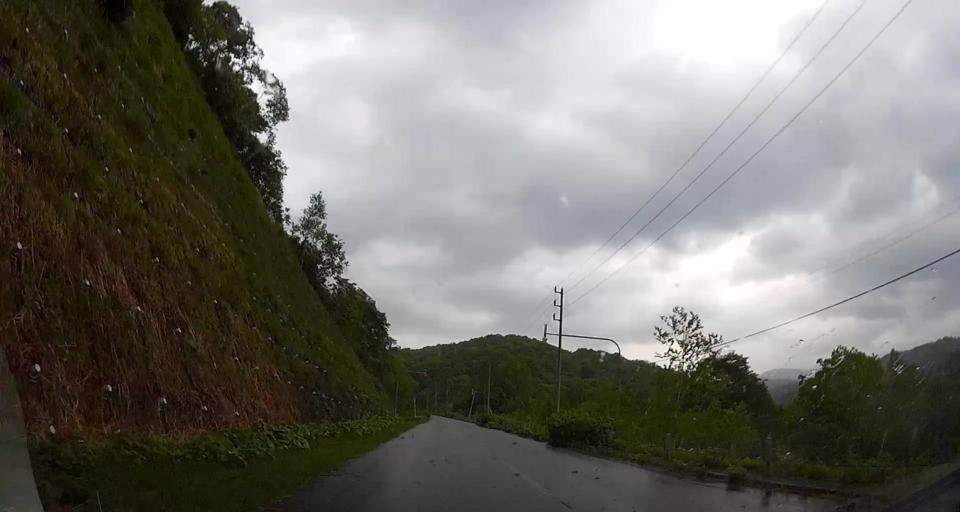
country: JP
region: Hokkaido
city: Niseko Town
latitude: 42.9095
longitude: 140.9239
